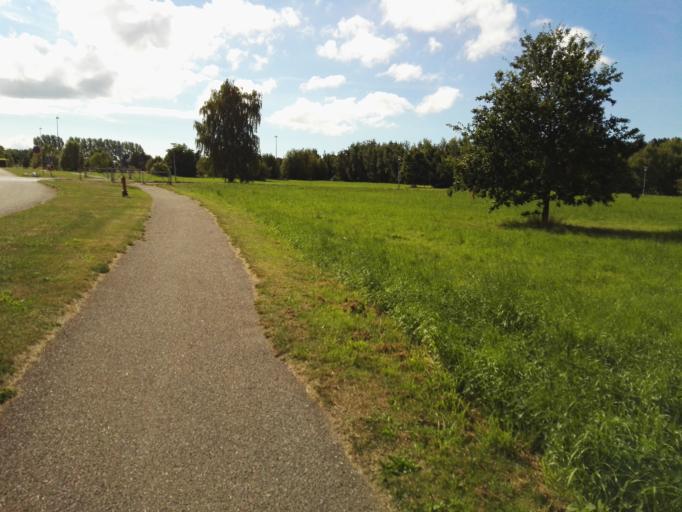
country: DK
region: Zealand
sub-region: Odsherred Kommune
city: Nykobing Sjaelland
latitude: 55.9357
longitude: 11.6767
